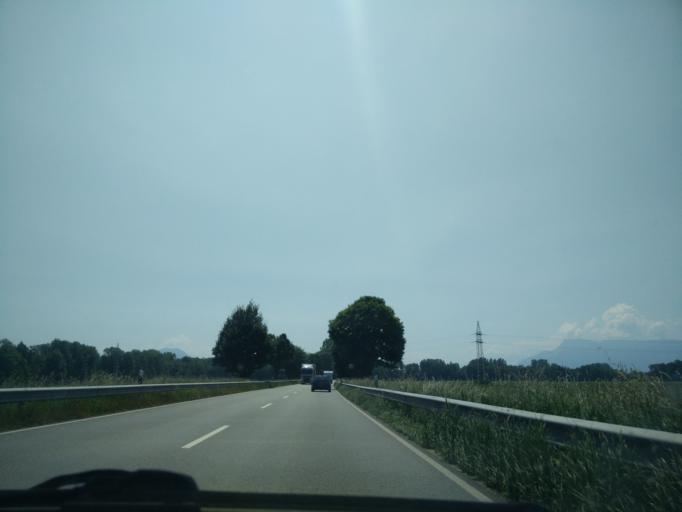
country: DE
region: Bavaria
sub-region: Upper Bavaria
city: Freilassing
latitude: 47.8914
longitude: 12.9613
